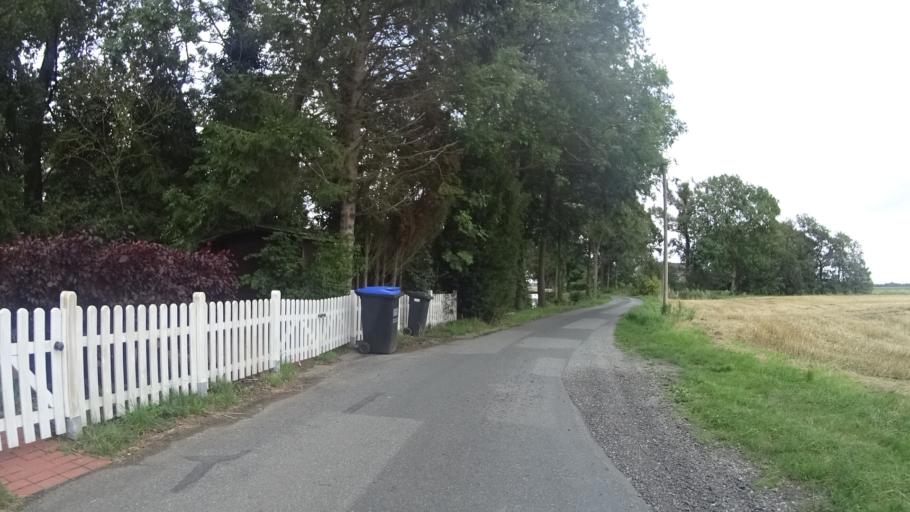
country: DE
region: Lower Saxony
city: Osten
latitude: 53.6952
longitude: 9.2303
